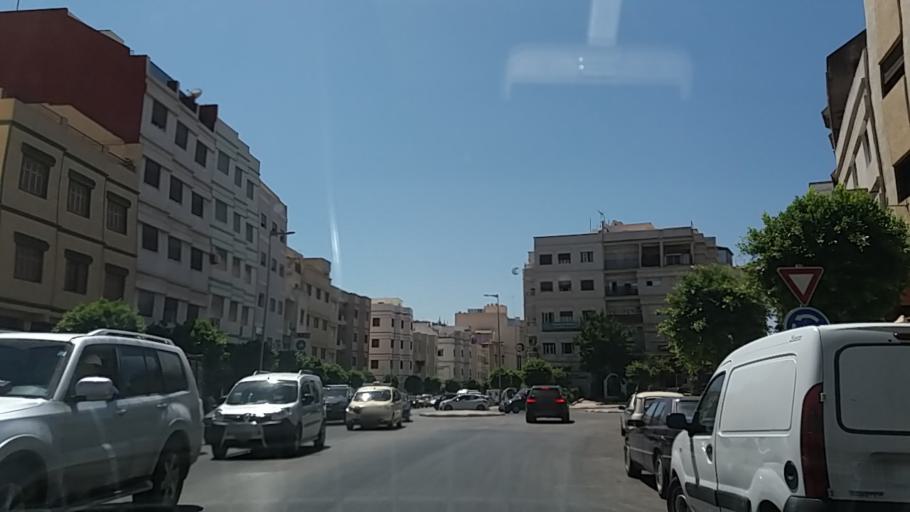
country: MA
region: Tanger-Tetouan
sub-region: Tanger-Assilah
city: Tangier
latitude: 35.7589
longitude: -5.8018
